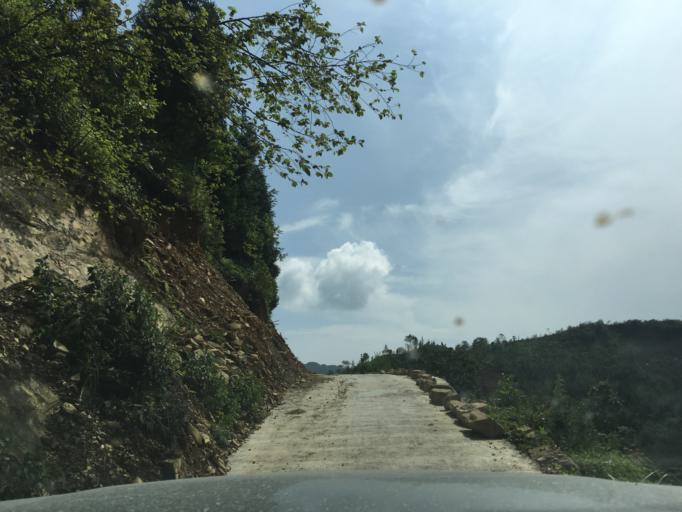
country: CN
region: Guangxi Zhuangzu Zizhiqu
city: Xinzhou
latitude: 24.9691
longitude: 105.6209
